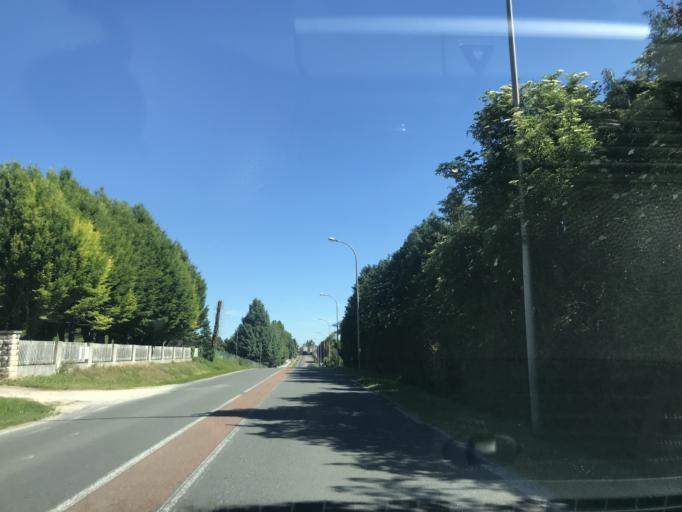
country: FR
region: Poitou-Charentes
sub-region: Departement de la Charente
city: Barbezieux-Saint-Hilaire
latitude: 45.4642
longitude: -0.1518
